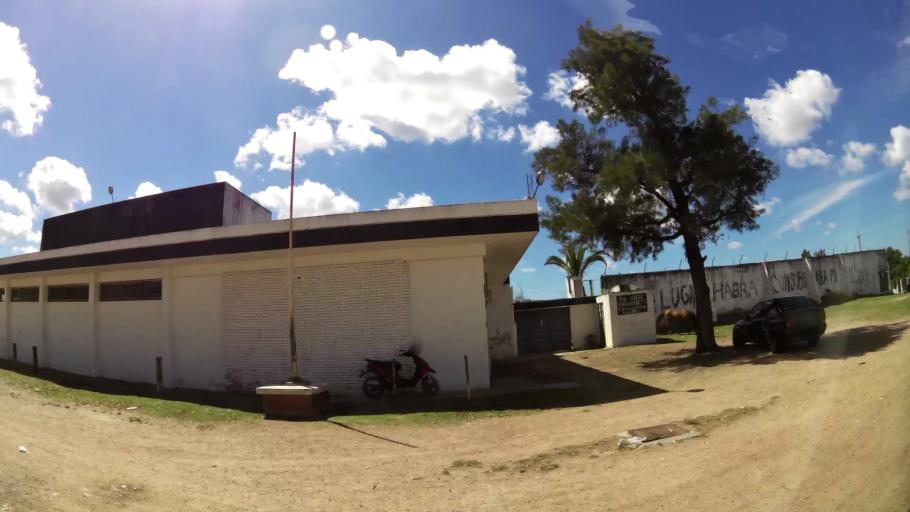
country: UY
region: Montevideo
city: Montevideo
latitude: -34.8387
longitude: -56.1338
